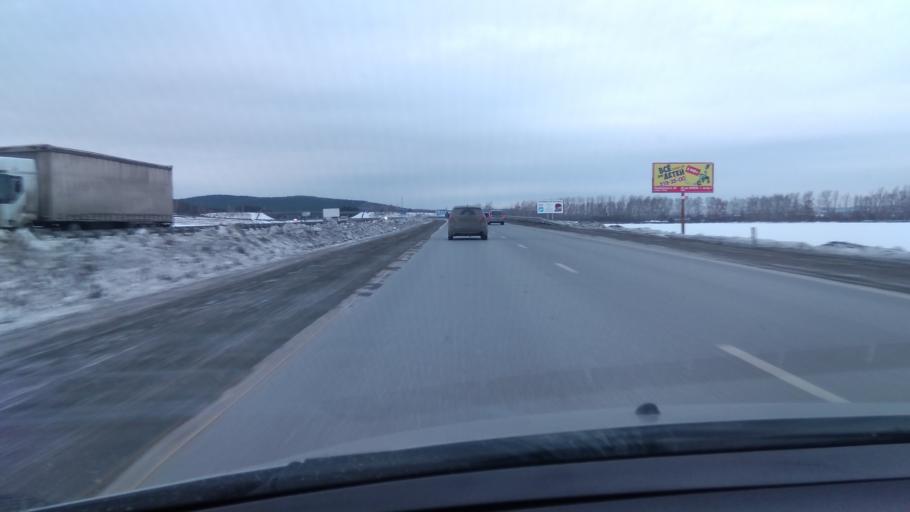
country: RU
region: Sverdlovsk
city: Aramil
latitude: 56.6896
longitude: 60.7658
